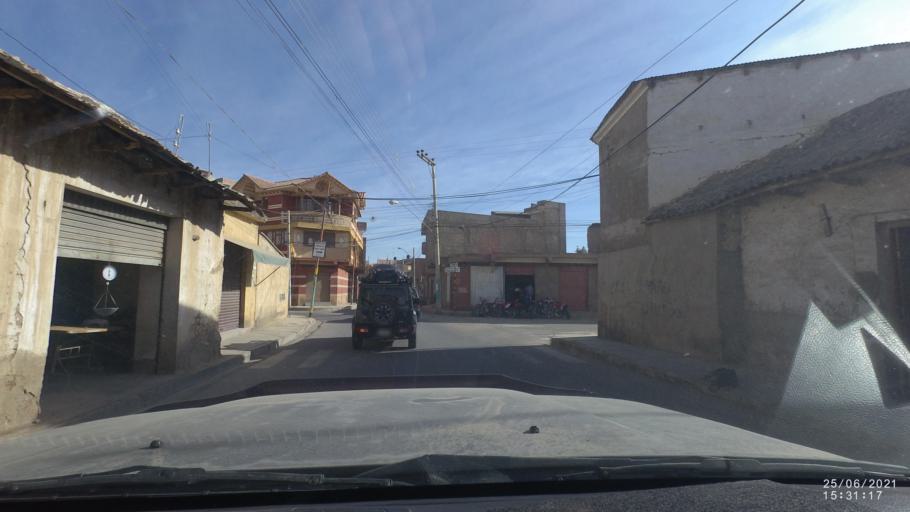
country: BO
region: Cochabamba
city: Cliza
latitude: -17.5891
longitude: -65.9344
